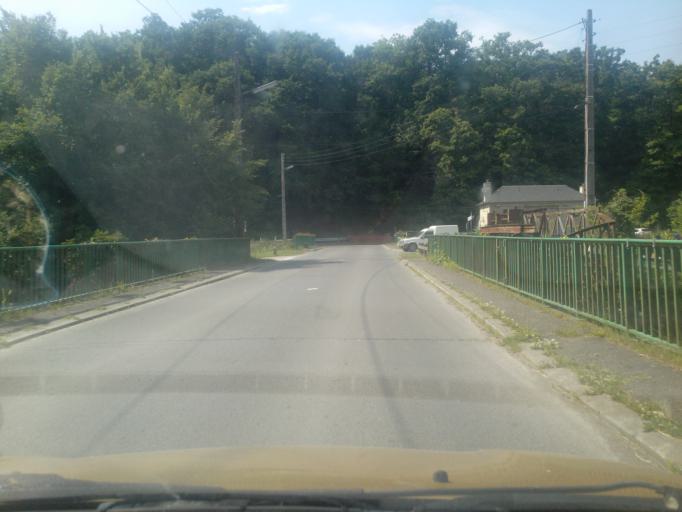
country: FR
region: Brittany
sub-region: Departement d'Ille-et-Vilaine
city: Saint-Medard-sur-Ille
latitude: 48.2477
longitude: -1.6671
